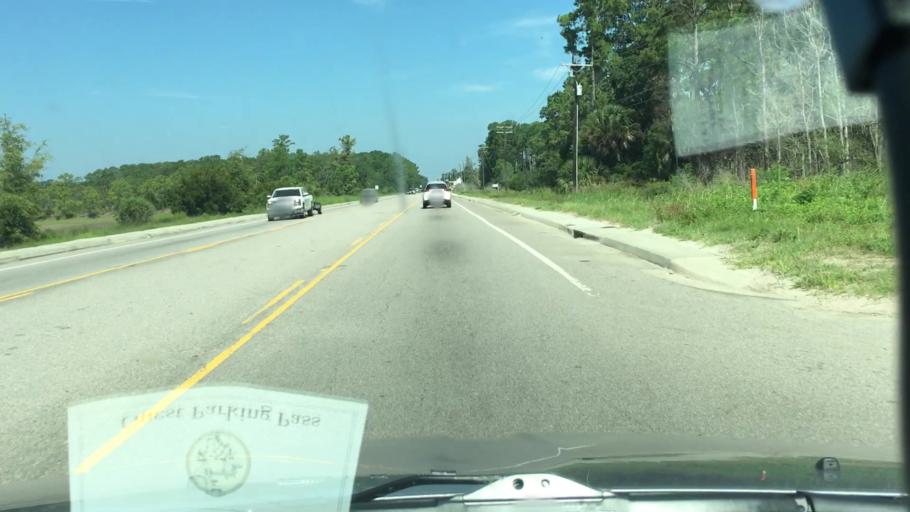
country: US
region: South Carolina
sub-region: Beaufort County
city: Beaufort
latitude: 32.4041
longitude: -80.6309
